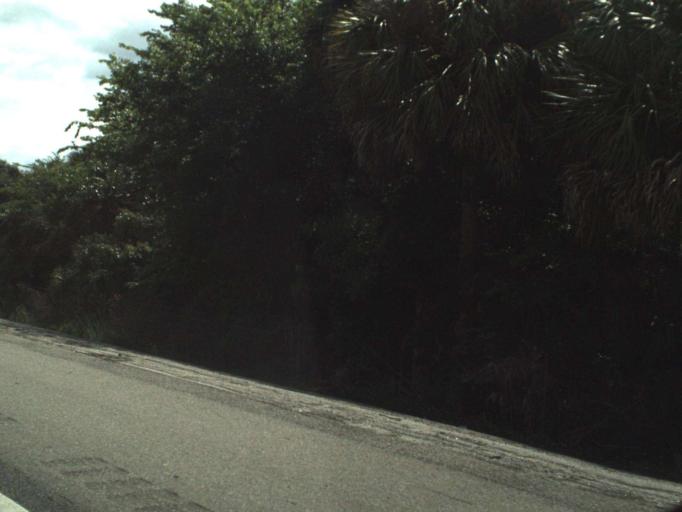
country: US
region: Florida
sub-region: Volusia County
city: DeBary
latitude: 28.8485
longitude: -81.3060
